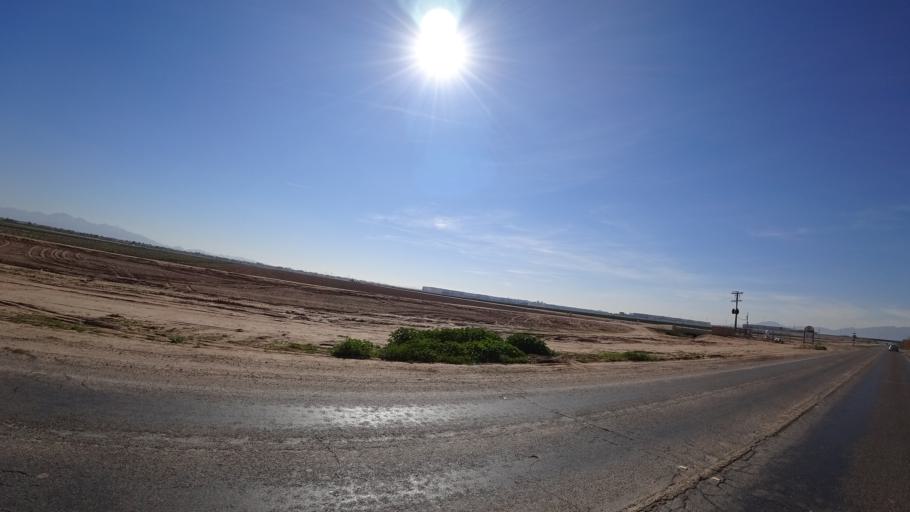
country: US
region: Arizona
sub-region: Maricopa County
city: Litchfield Park
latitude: 33.5082
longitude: -112.4081
